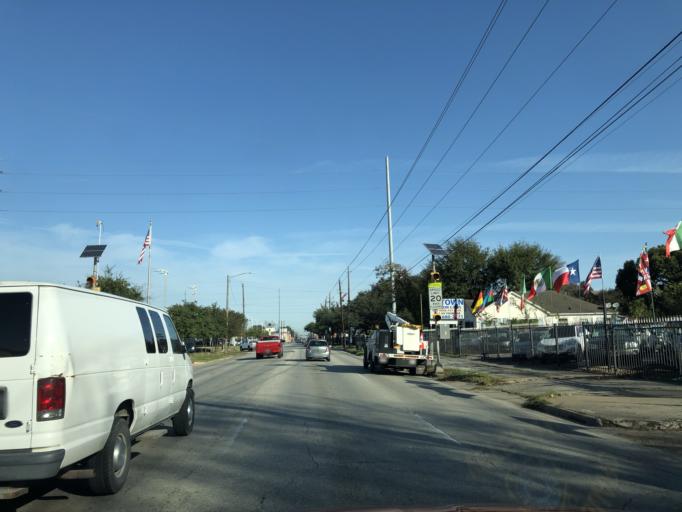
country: US
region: Texas
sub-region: Harris County
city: Houston
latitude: 29.7915
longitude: -95.4099
